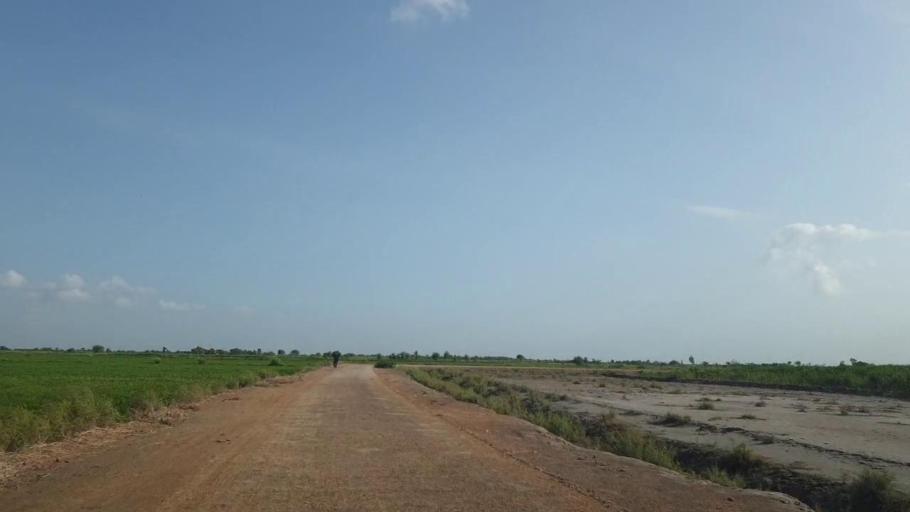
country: PK
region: Sindh
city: Kadhan
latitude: 24.6118
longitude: 69.0919
